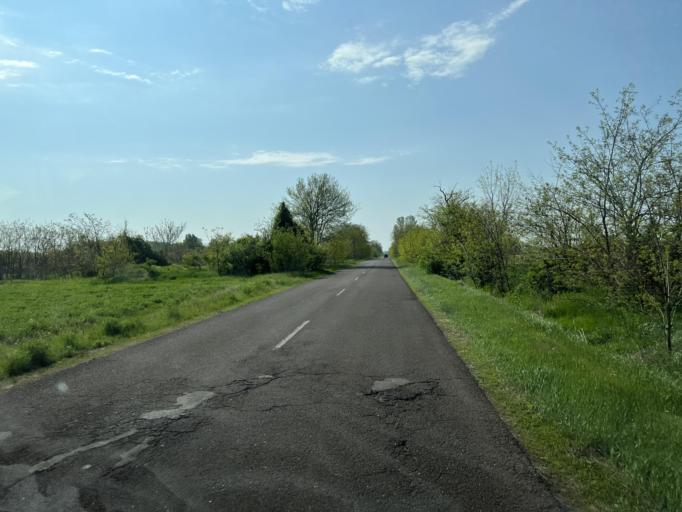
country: HU
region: Pest
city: Jaszkarajeno
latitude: 47.0235
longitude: 20.0387
